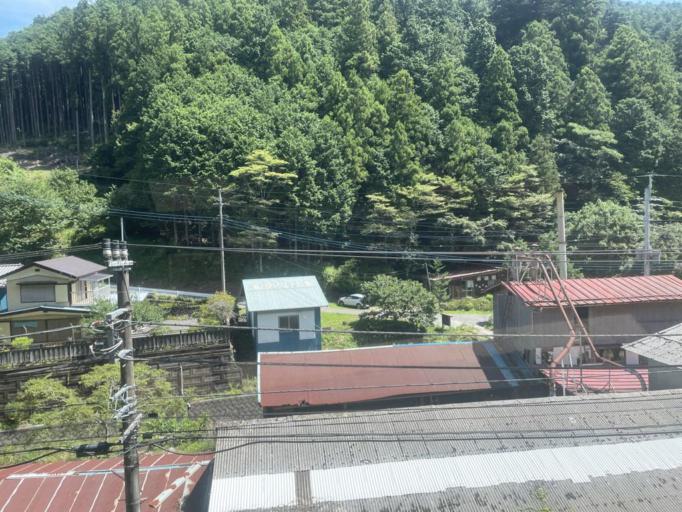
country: JP
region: Saitama
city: Morohongo
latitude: 35.9318
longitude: 139.2029
